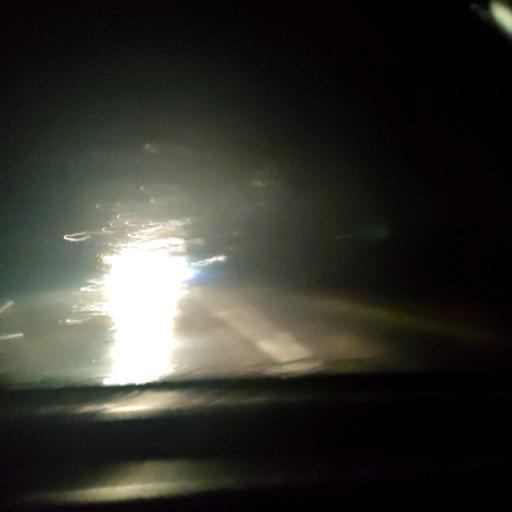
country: RU
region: Voronezj
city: Devitsa
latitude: 51.5862
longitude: 38.9766
